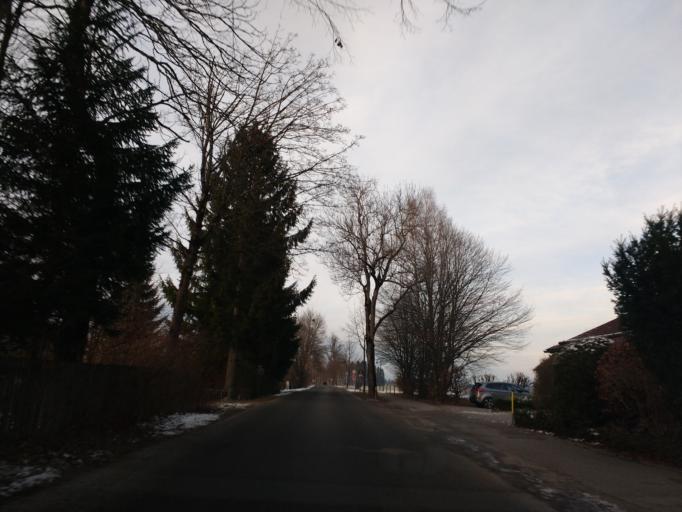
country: DE
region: Bavaria
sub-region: Swabia
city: Schwangau
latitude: 47.5613
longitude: 10.7387
